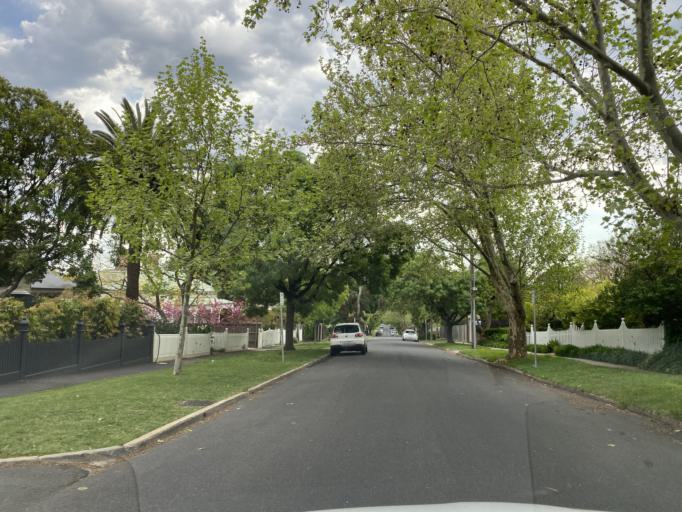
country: AU
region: Victoria
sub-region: Boroondara
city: Canterbury
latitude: -37.8286
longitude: 145.0799
